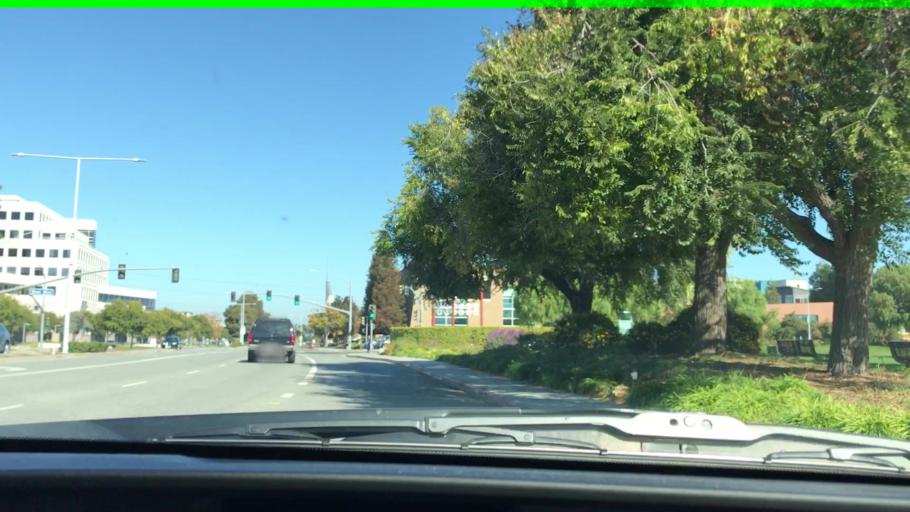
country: US
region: California
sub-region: San Mateo County
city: Foster City
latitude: 37.5578
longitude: -122.2720
